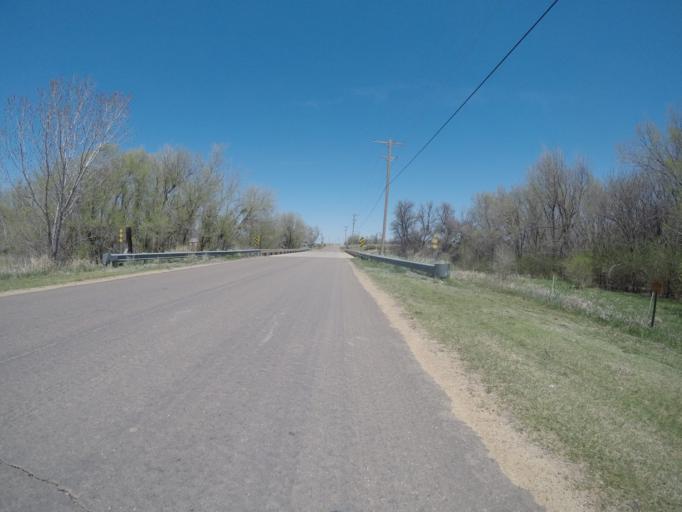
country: US
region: Kansas
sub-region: Pratt County
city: Pratt
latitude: 37.6393
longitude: -98.7668
